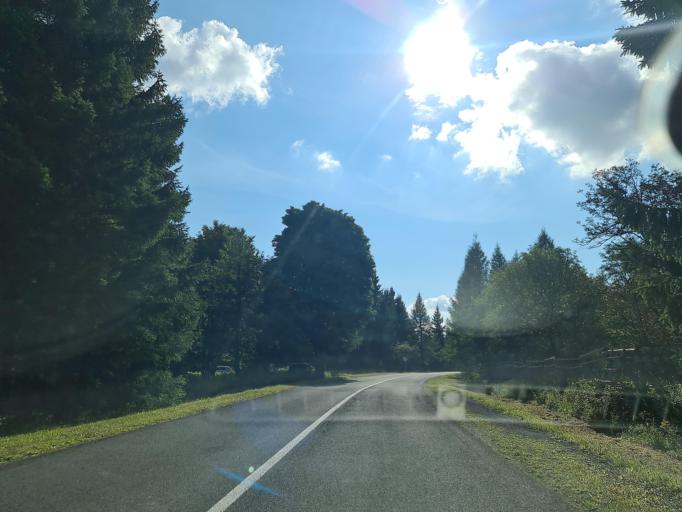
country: CZ
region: Ustecky
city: Mezibori
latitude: 50.6361
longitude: 13.5422
